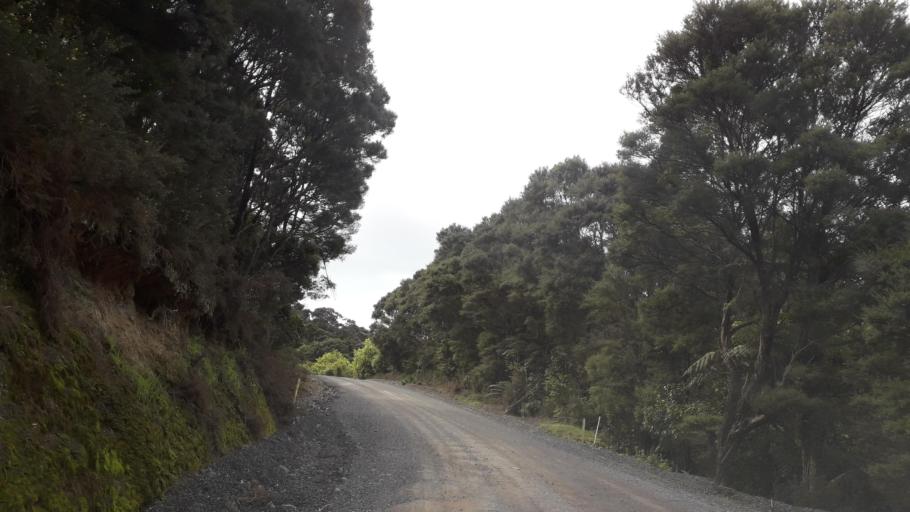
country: NZ
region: Northland
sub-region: Far North District
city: Paihia
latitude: -35.3052
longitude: 174.2206
